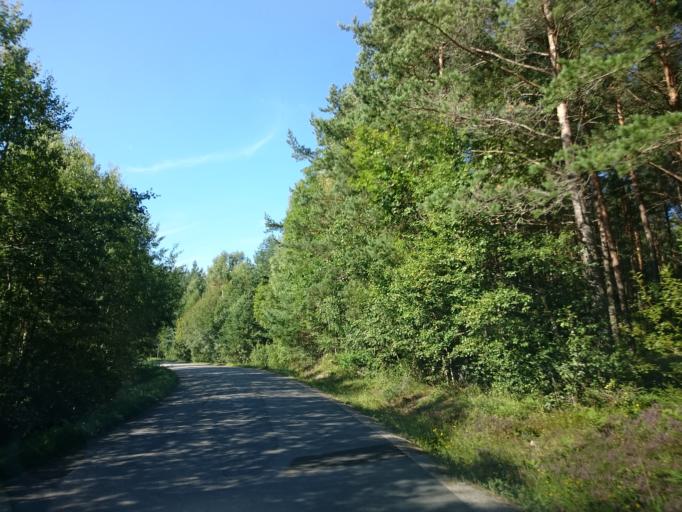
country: SE
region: Soedermanland
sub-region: Nykopings Kommun
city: Olstorp
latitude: 58.6493
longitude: 16.6410
